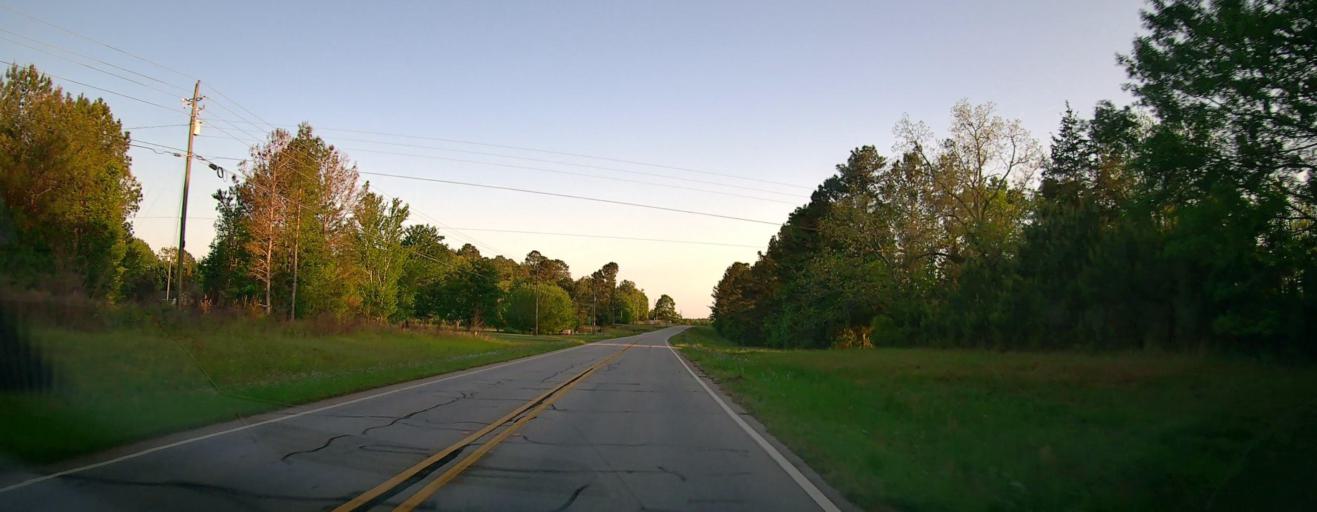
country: US
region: Georgia
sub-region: Newton County
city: Oakwood
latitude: 33.5134
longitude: -83.9481
